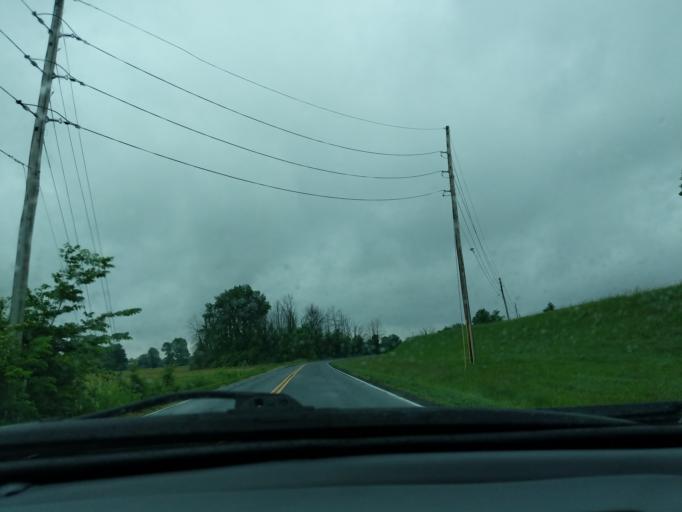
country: US
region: Indiana
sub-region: Hamilton County
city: Cicero
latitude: 40.0970
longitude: -86.0315
